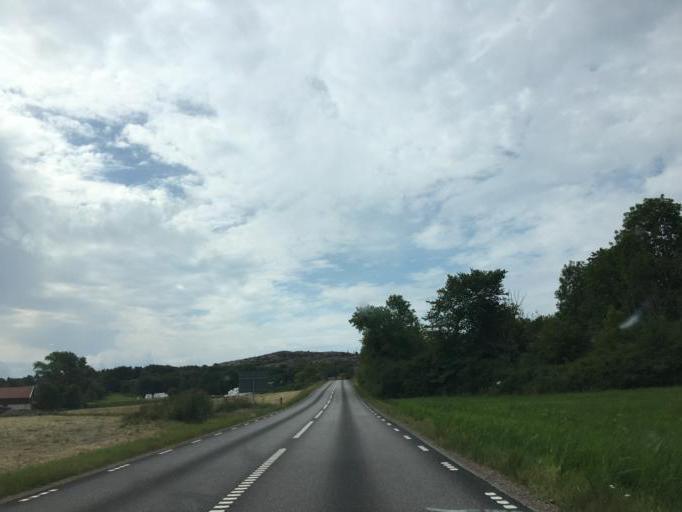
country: SE
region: Vaestra Goetaland
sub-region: Sotenas Kommun
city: Hunnebostrand
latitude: 58.4192
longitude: 11.2893
